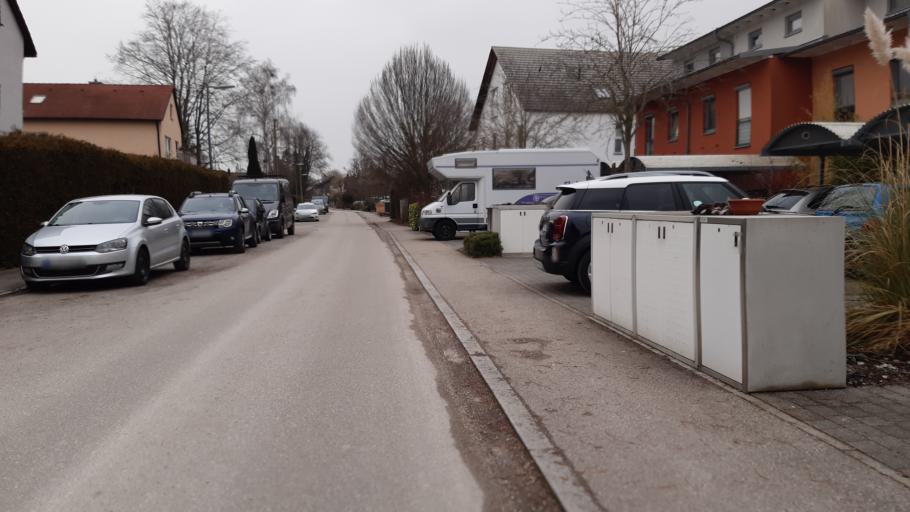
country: DE
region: Bavaria
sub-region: Upper Bavaria
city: Karlsfeld
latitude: 48.1962
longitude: 11.5148
